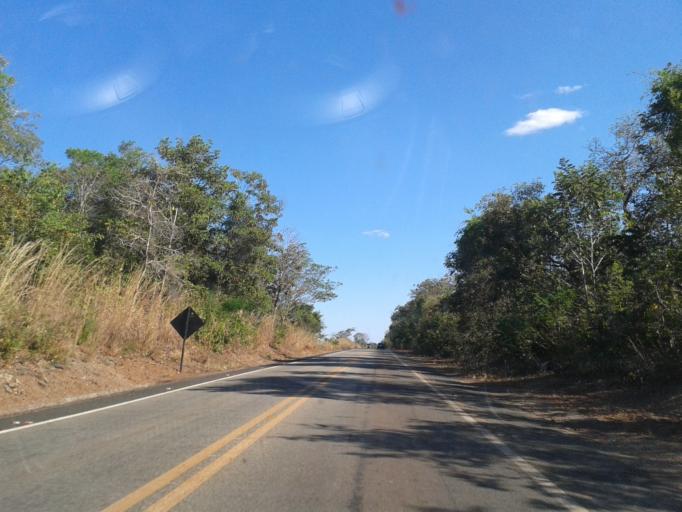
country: BR
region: Goias
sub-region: Mozarlandia
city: Mozarlandia
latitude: -14.6782
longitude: -50.5376
